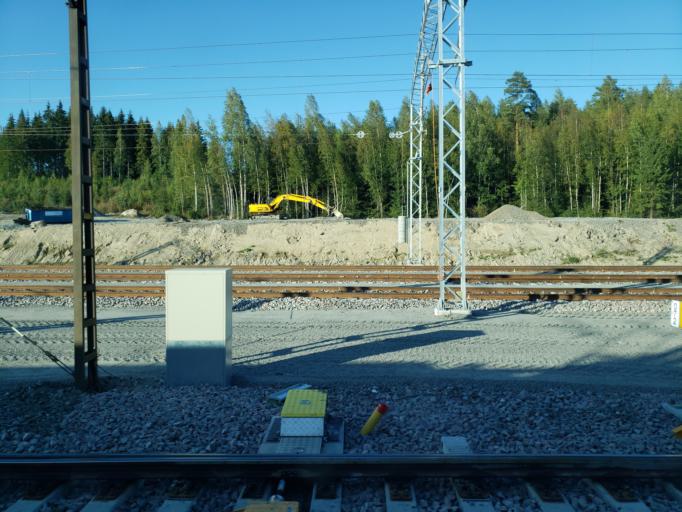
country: FI
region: South Karelia
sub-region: Lappeenranta
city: Lappeenranta
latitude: 60.8601
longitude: 28.3201
